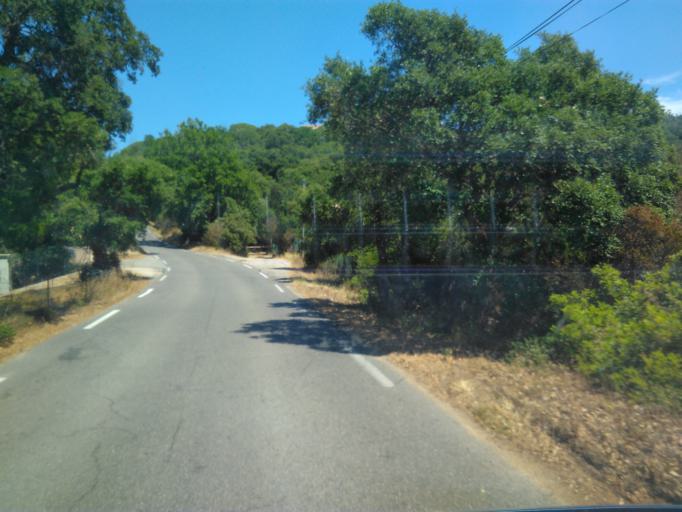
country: FR
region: Provence-Alpes-Cote d'Azur
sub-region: Departement du Var
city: Gassin
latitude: 43.2187
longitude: 6.5865
